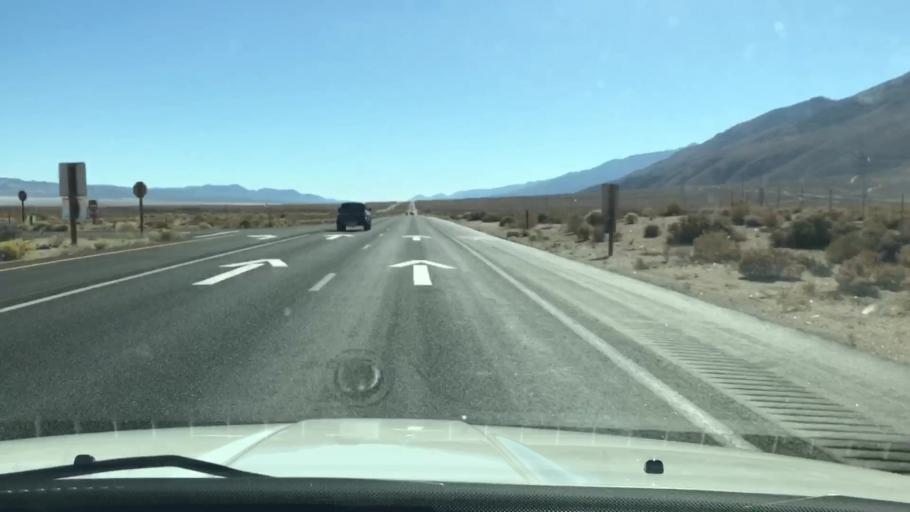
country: US
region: California
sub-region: Inyo County
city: Lone Pine
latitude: 36.4184
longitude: -118.0295
